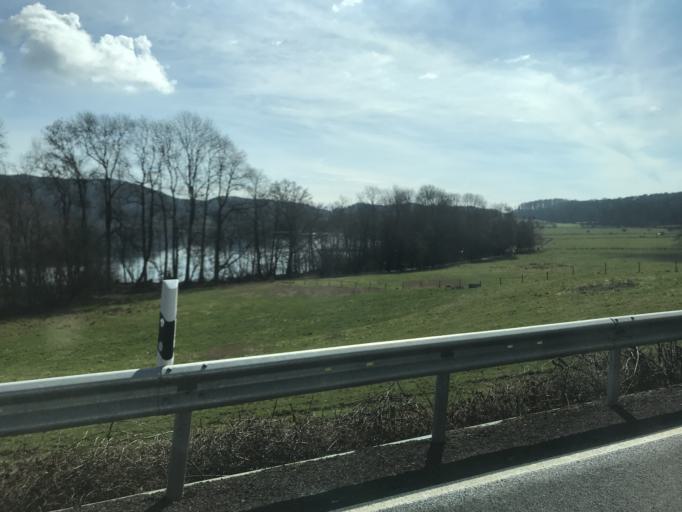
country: DE
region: Rheinland-Pfalz
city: Glees
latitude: 50.4086
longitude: 7.2537
